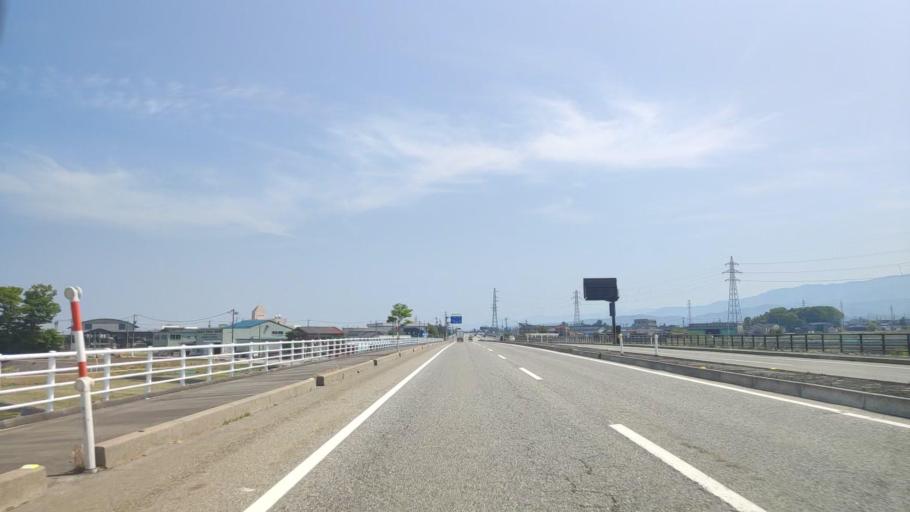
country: JP
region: Toyama
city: Namerikawa
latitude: 36.7604
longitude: 137.3657
